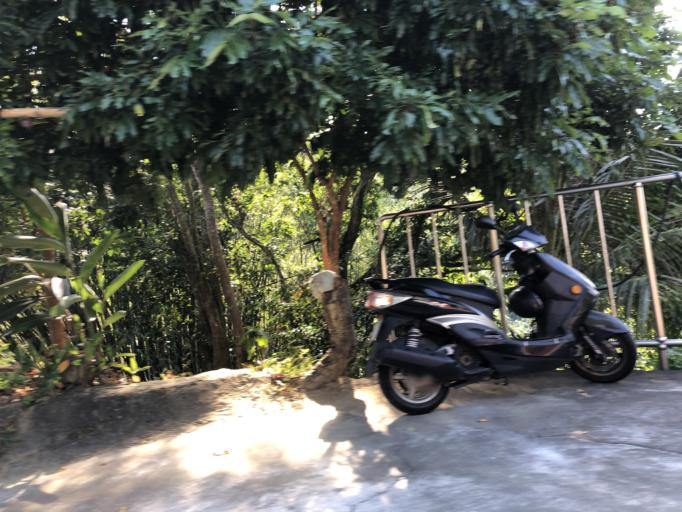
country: TW
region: Taiwan
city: Yujing
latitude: 23.0299
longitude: 120.3843
